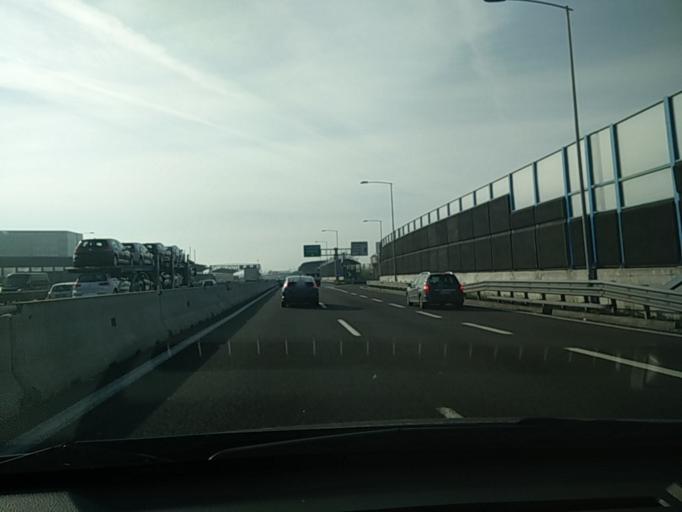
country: IT
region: Emilia-Romagna
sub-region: Provincia di Bologna
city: San Lazzaro
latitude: 44.4965
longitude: 11.3883
